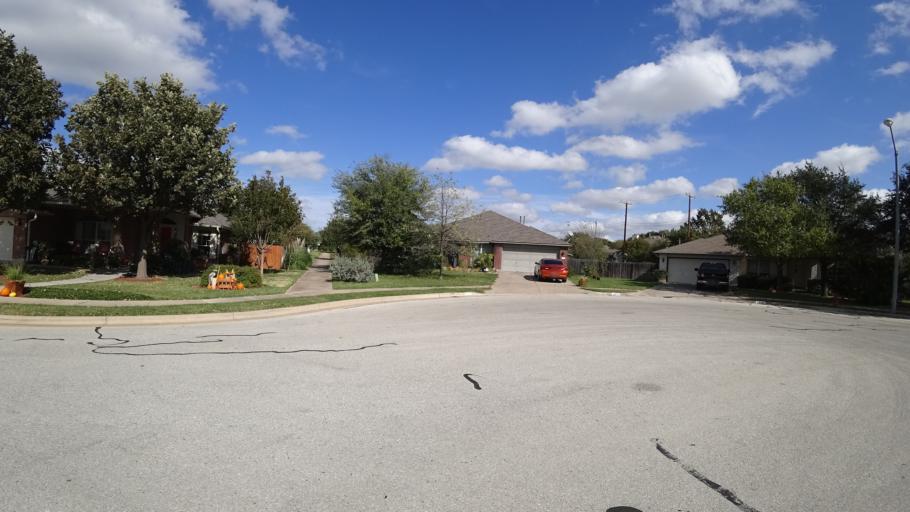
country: US
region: Texas
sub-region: Travis County
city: Windemere
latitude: 30.4709
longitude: -97.6550
